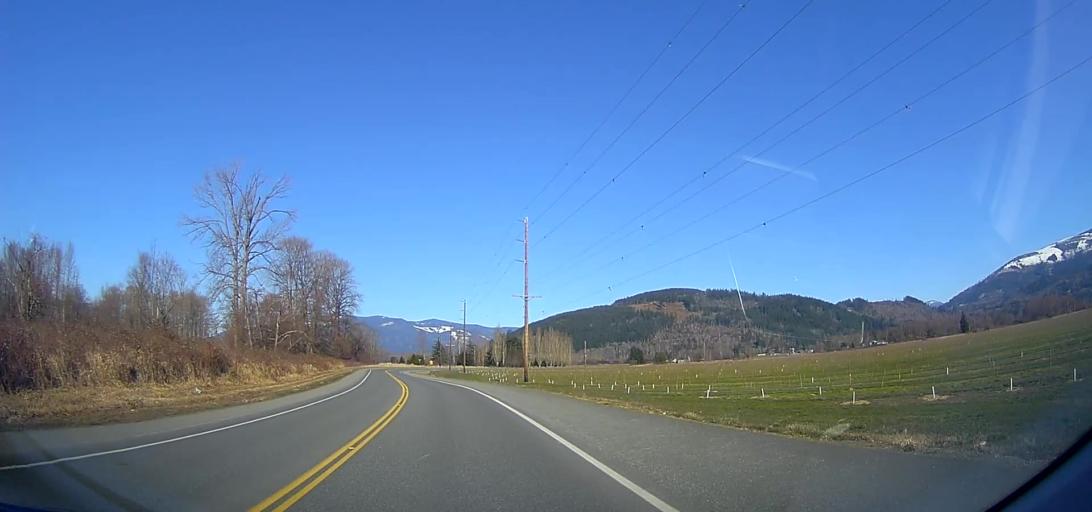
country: US
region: Washington
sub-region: Skagit County
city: Clear Lake
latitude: 48.4657
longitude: -122.2573
